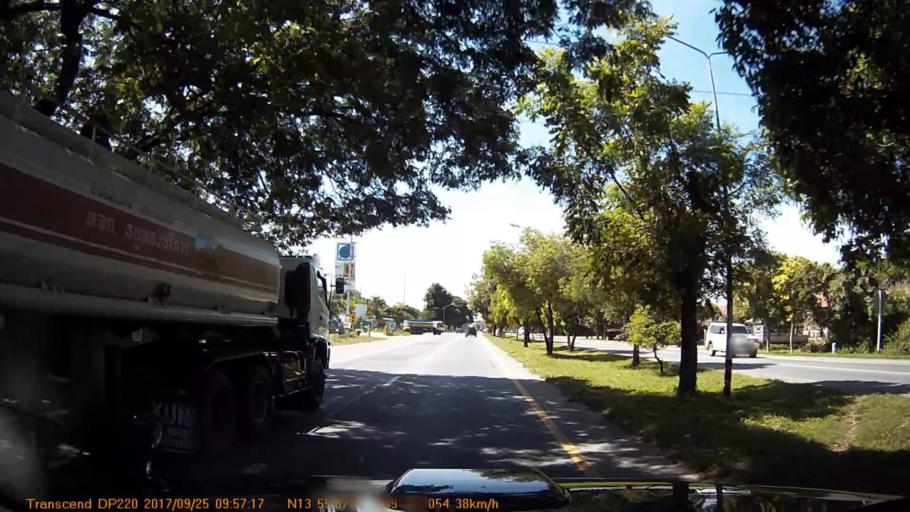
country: TH
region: Kanchanaburi
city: Tha Maka
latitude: 13.9312
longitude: 99.7617
